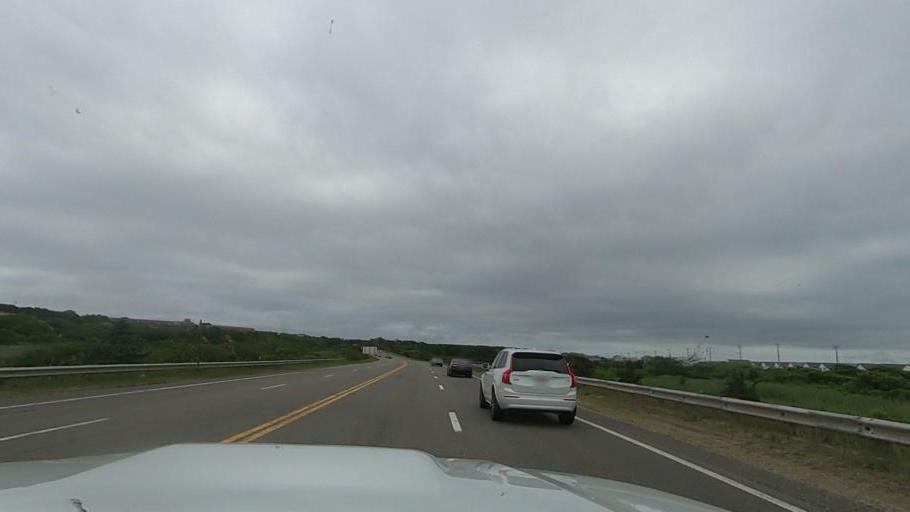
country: US
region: Massachusetts
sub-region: Barnstable County
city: Provincetown
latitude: 42.0507
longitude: -70.1175
